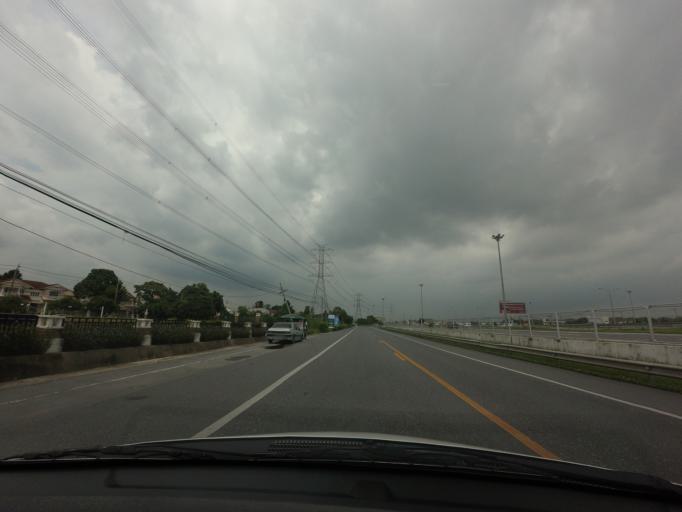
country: TH
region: Bangkok
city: Saphan Sung
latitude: 13.7358
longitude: 100.7020
